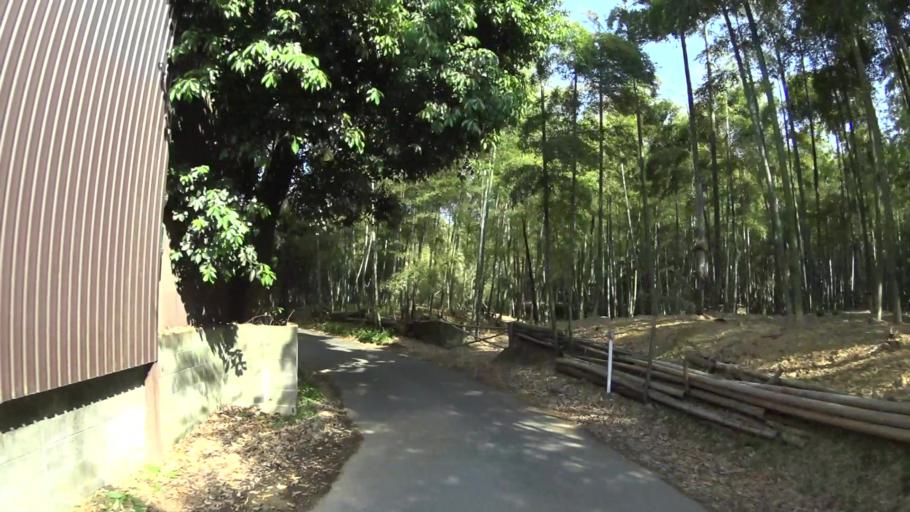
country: JP
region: Kyoto
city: Muko
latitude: 34.9444
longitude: 135.6791
